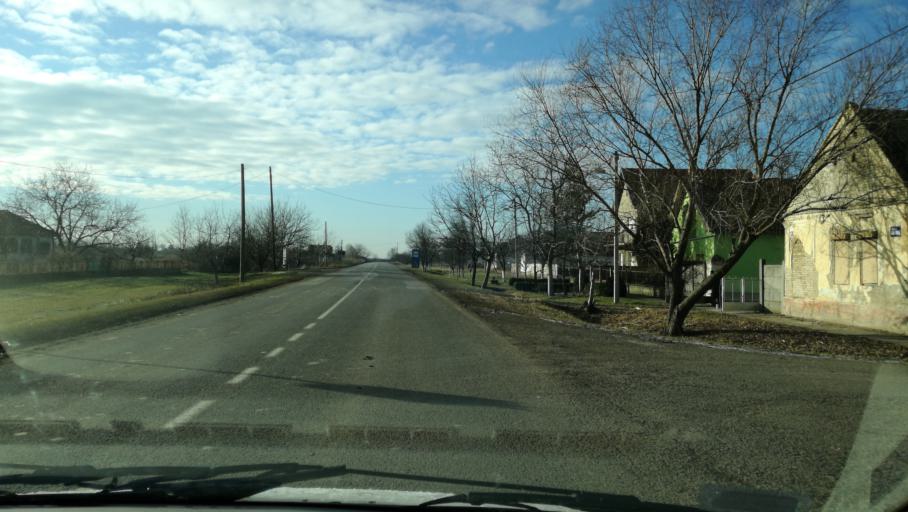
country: RS
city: Tiszahegyes
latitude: 45.8232
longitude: 20.3218
